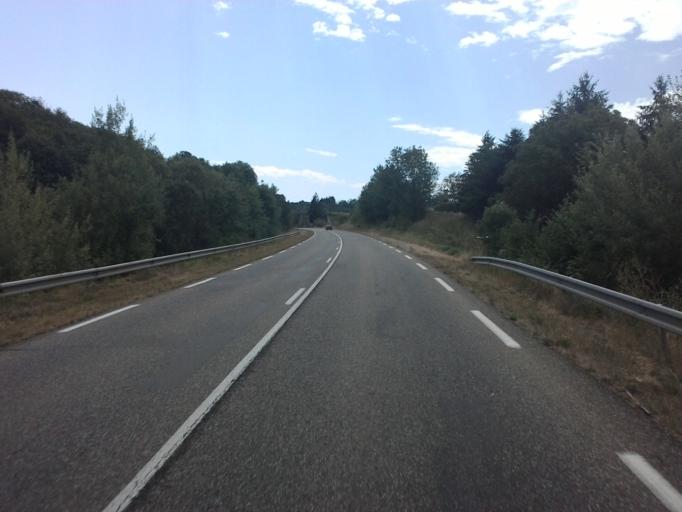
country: FR
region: Franche-Comte
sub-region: Departement du Jura
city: Saint-Amour
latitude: 46.4442
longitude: 5.3475
